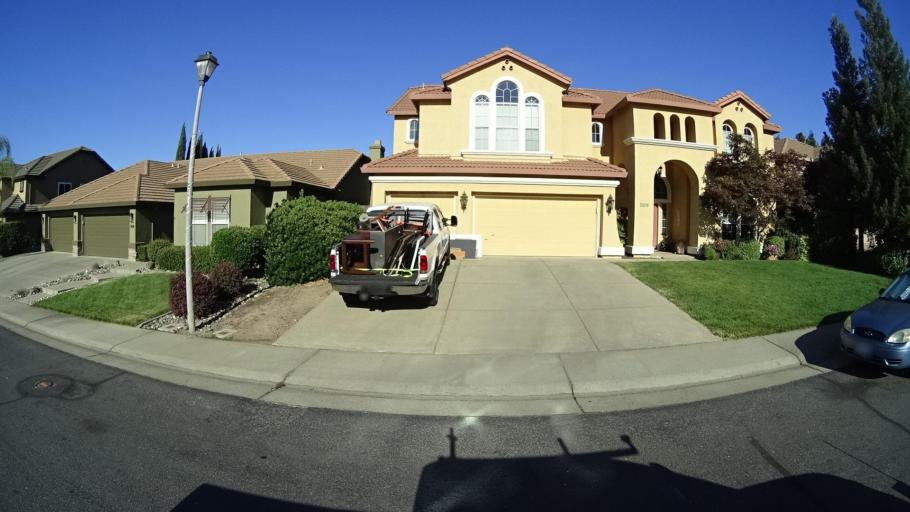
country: US
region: California
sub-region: Placer County
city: Rocklin
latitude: 38.8228
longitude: -121.2801
